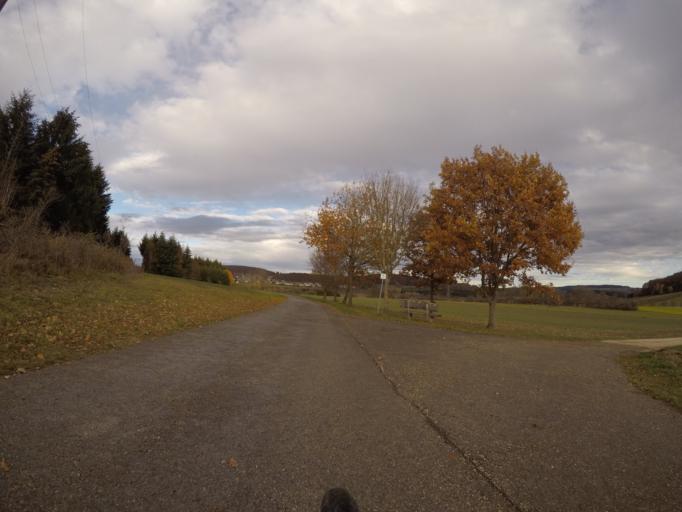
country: DE
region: Baden-Wuerttemberg
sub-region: Tuebingen Region
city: Sankt Johann
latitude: 48.4420
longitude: 9.3318
